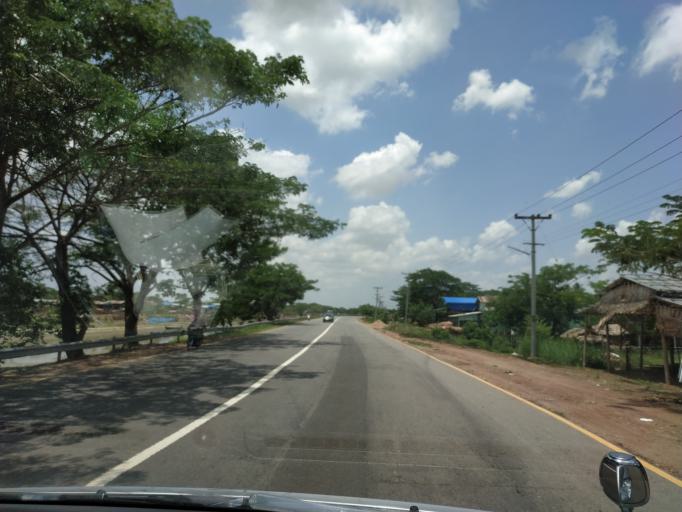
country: MM
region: Bago
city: Thanatpin
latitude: 17.5047
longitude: 96.7100
